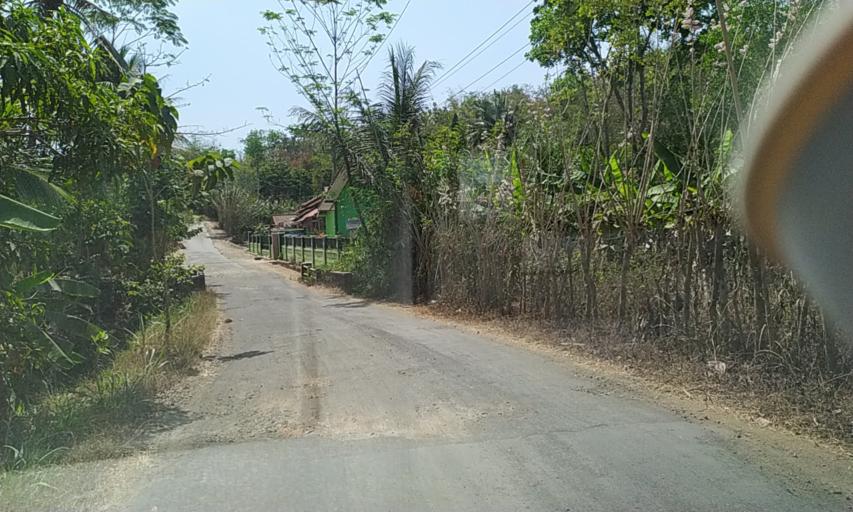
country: ID
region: Central Java
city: Karanggintung
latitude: -7.4588
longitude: 108.8637
